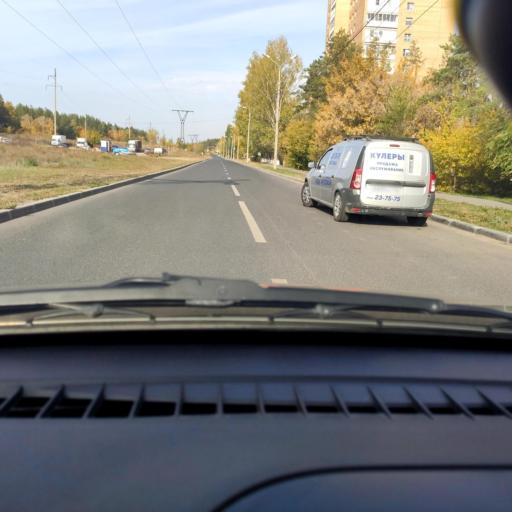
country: RU
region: Samara
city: Zhigulevsk
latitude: 53.4774
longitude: 49.4533
